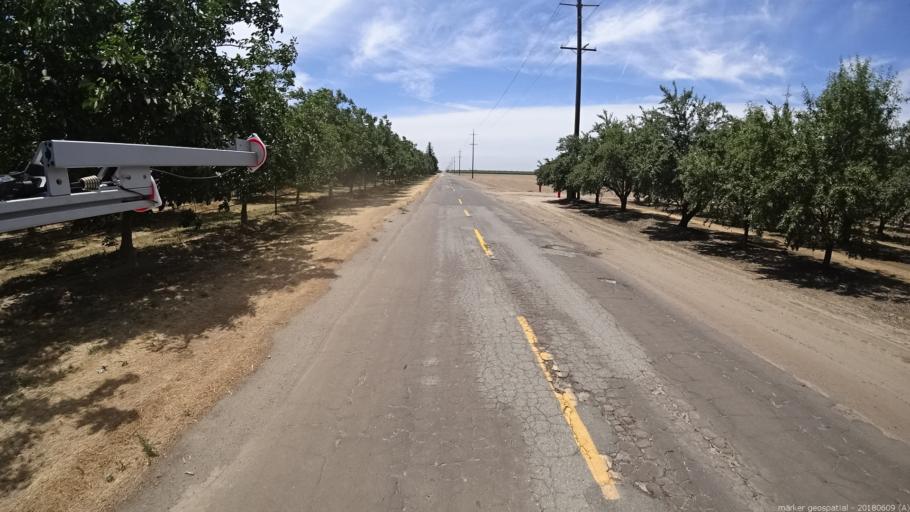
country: US
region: California
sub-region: Madera County
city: Parkwood
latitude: 36.9165
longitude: -120.0785
